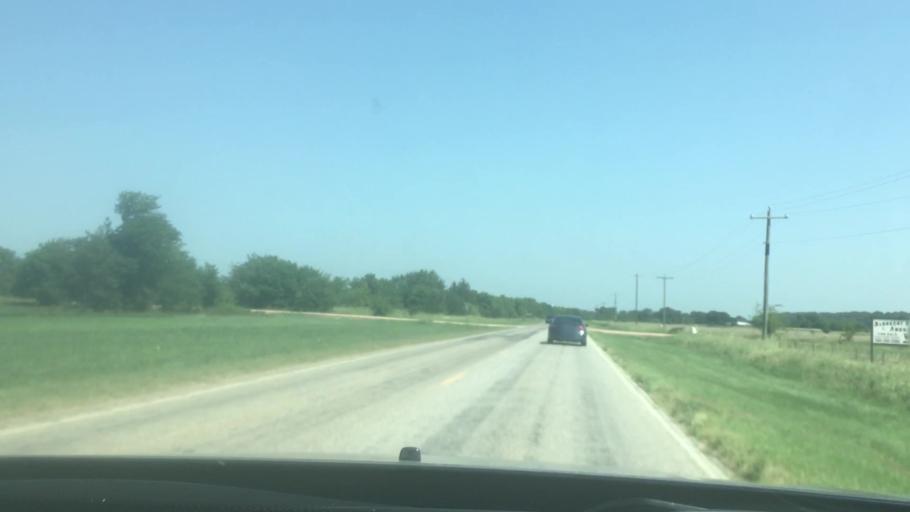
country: US
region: Oklahoma
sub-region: Johnston County
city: Tishomingo
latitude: 34.3447
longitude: -96.4227
